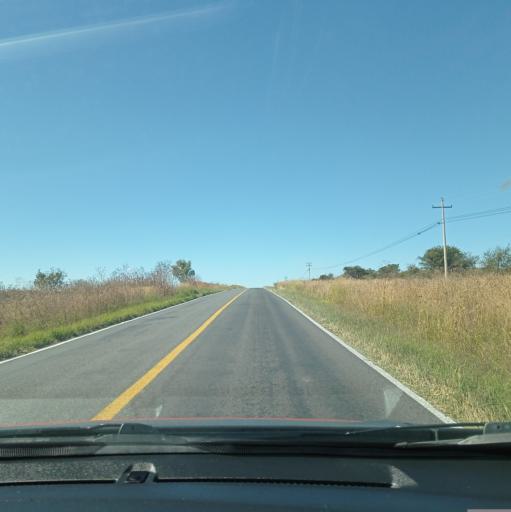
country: MX
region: Jalisco
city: San Diego de Alejandria
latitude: 21.0060
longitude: -102.0532
